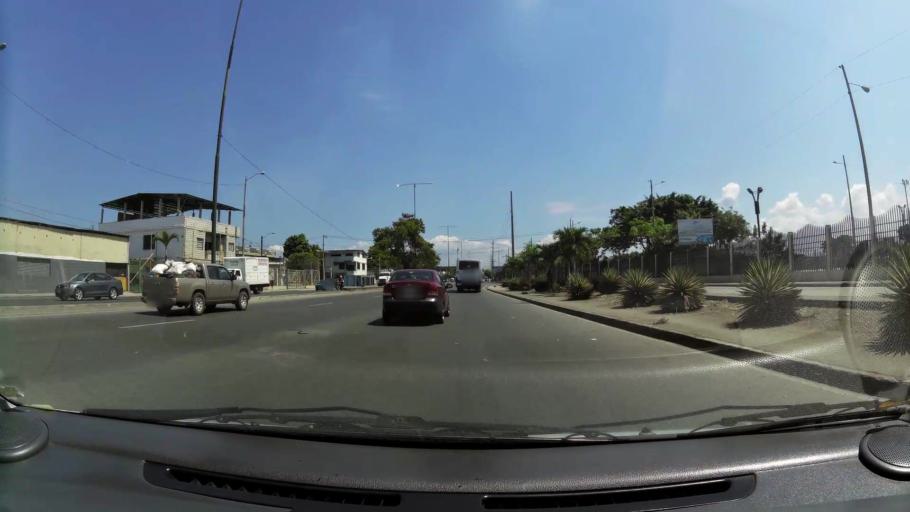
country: EC
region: Guayas
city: Guayaquil
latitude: -2.2388
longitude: -79.8997
